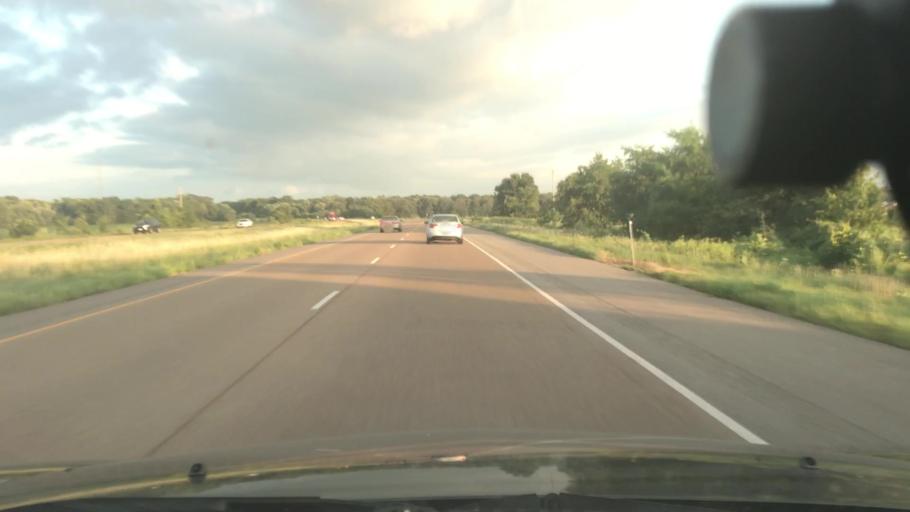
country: US
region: Illinois
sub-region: Washington County
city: Okawville
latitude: 38.4642
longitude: -89.5702
